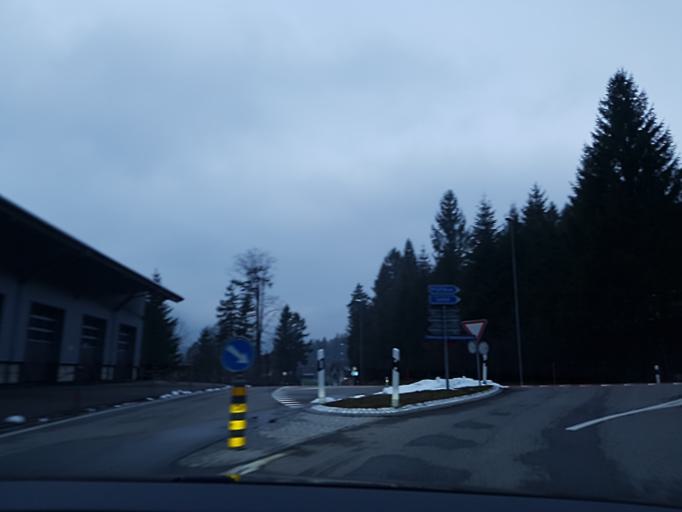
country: CH
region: Schwyz
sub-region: Bezirk Schwyz
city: Goldau
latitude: 47.0517
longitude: 8.5628
